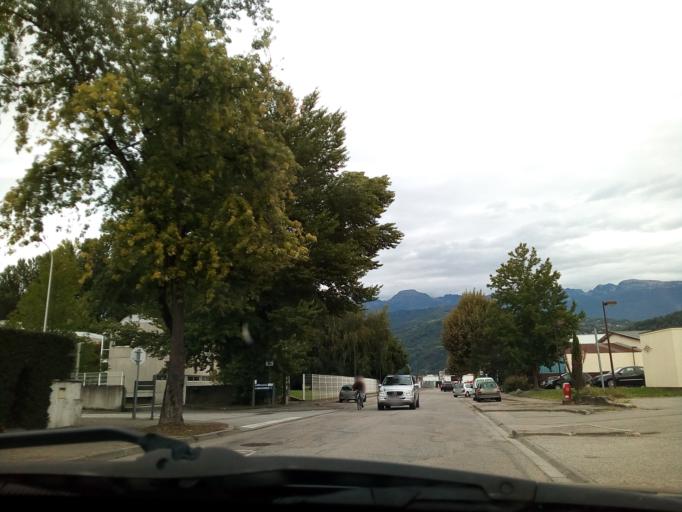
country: FR
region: Rhone-Alpes
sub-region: Departement de l'Isere
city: Saint-Martin-d'Heres
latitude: 45.1858
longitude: 5.7659
